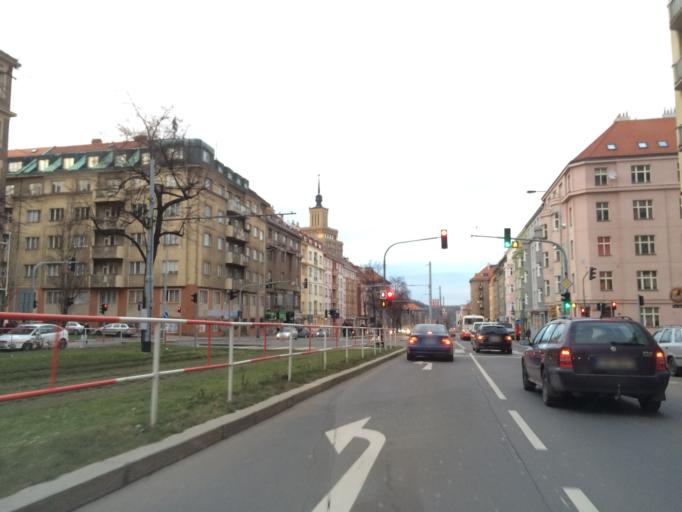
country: CZ
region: Praha
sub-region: Praha 1
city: Mala Strana
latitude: 50.1066
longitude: 14.3948
